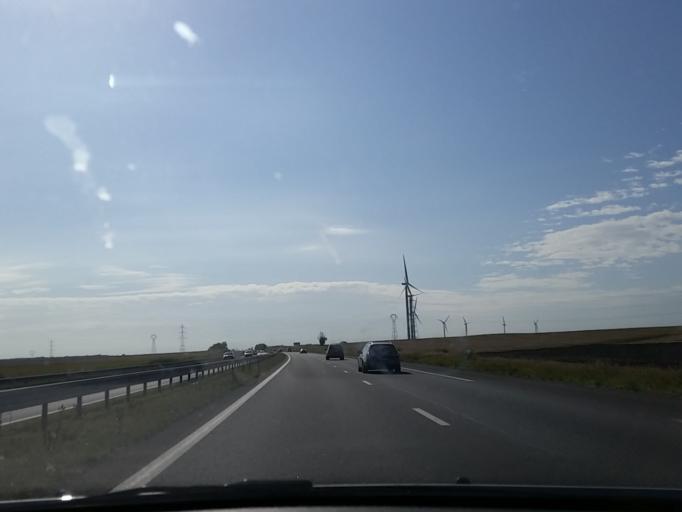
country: FR
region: Centre
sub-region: Departement du Cher
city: Mehun-sur-Yevre
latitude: 47.1084
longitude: 2.2075
